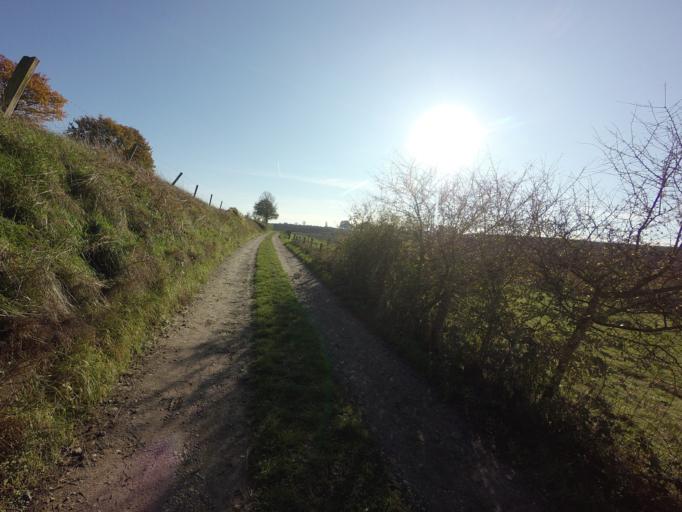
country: NL
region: Limburg
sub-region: Gemeente Simpelveld
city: Simpelveld
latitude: 50.8255
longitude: 5.9648
